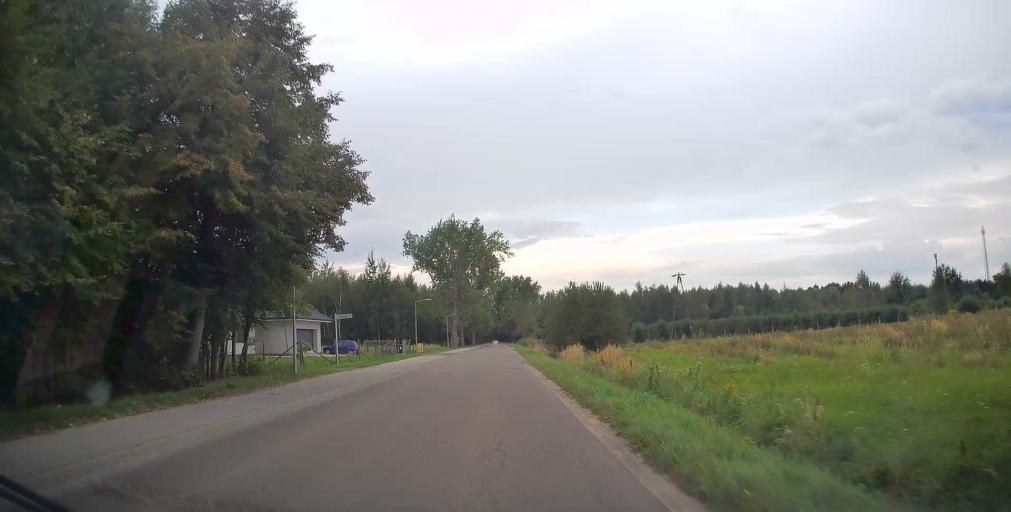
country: PL
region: Masovian Voivodeship
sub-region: Powiat bialobrzeski
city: Sucha
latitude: 51.6306
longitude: 20.9539
